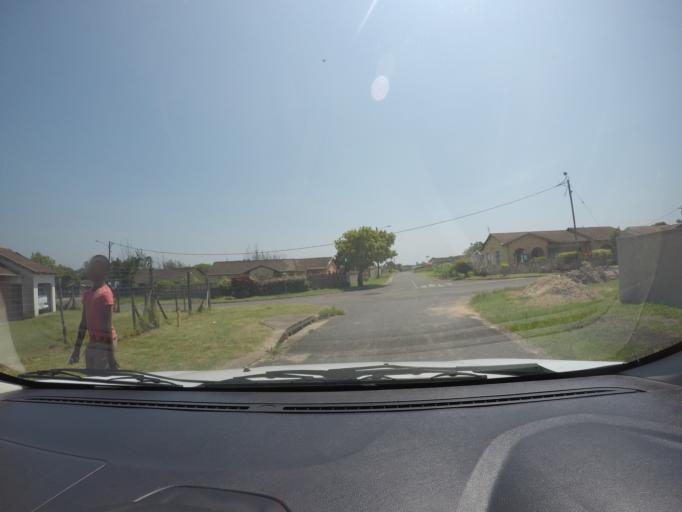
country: ZA
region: KwaZulu-Natal
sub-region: uThungulu District Municipality
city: eSikhawini
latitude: -28.8662
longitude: 31.9180
